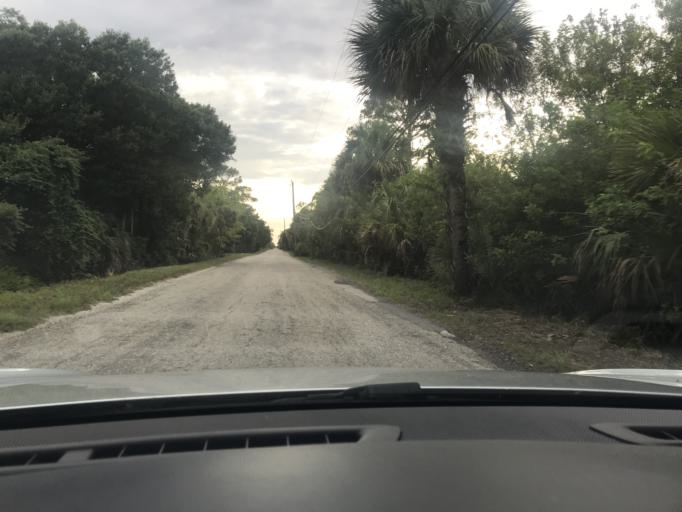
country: US
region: Florida
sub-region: Indian River County
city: Gifford
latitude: 27.6827
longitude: -80.4506
